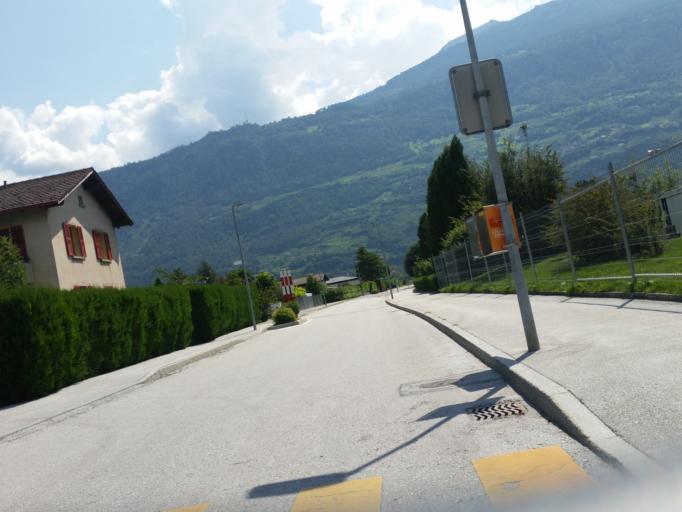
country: CH
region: Valais
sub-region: Conthey District
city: Ardon
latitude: 46.2086
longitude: 7.2586
